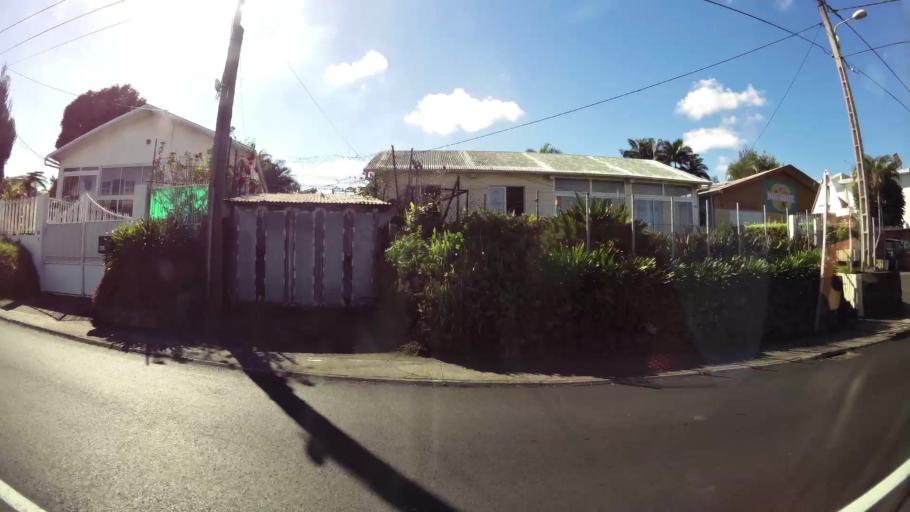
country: RE
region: Reunion
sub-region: Reunion
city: Le Tampon
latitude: -21.2720
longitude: 55.5246
